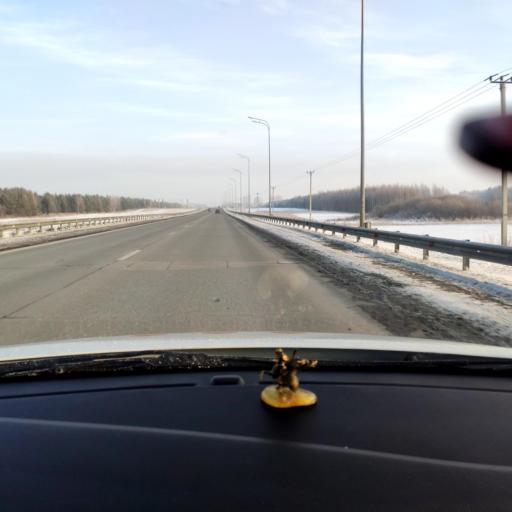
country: RU
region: Tatarstan
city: Stolbishchi
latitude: 55.6668
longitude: 49.1695
